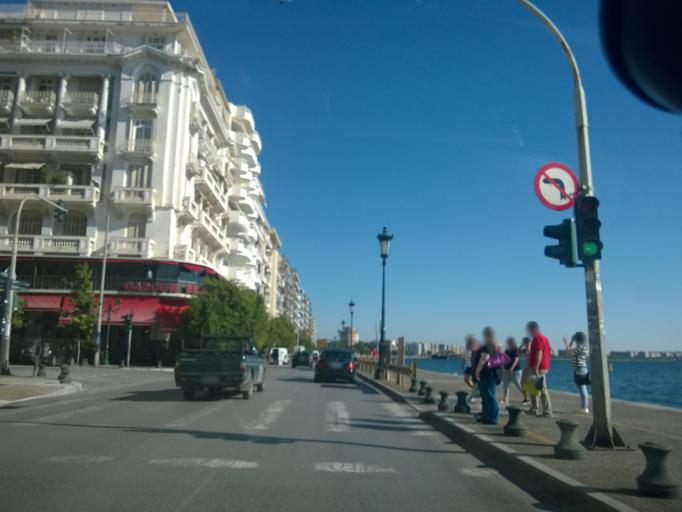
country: GR
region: Central Macedonia
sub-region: Nomos Thessalonikis
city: Thessaloniki
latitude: 40.6306
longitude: 22.9428
